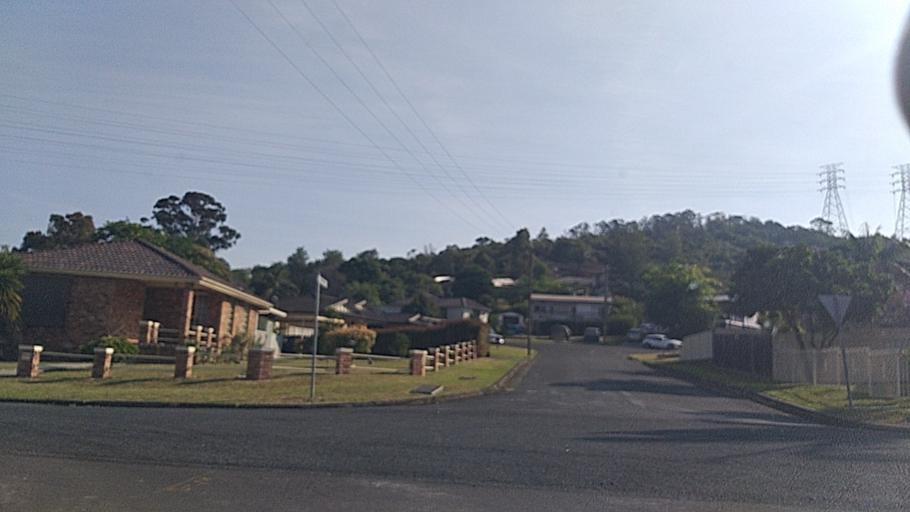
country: AU
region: New South Wales
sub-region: Wollongong
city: Berkeley
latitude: -34.4728
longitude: 150.8443
